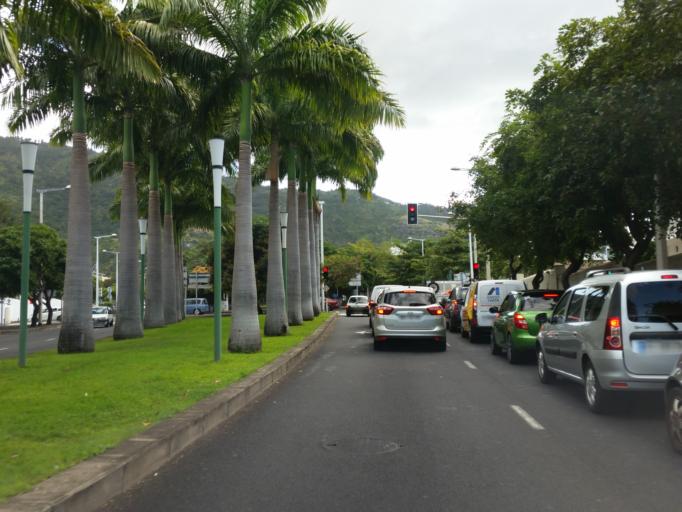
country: RE
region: Reunion
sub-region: Reunion
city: Saint-Denis
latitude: -20.8888
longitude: 55.4495
